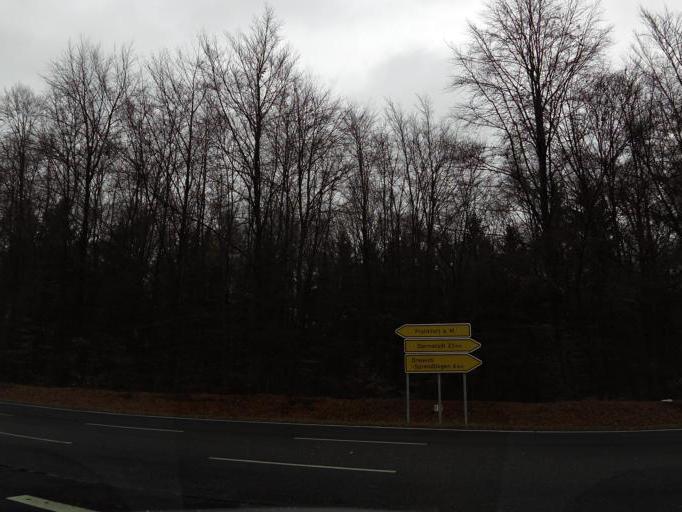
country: DE
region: Hesse
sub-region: Regierungsbezirk Darmstadt
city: Neu Isenburg
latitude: 50.0621
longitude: 8.6886
